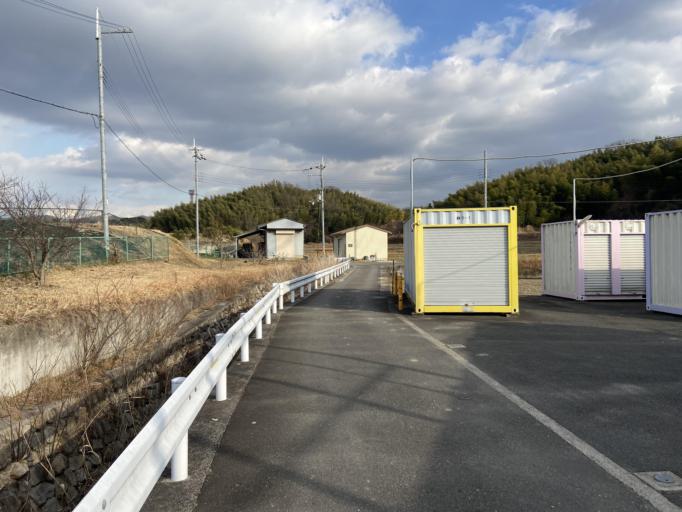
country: JP
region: Osaka
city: Neyagawa
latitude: 34.7604
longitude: 135.6583
